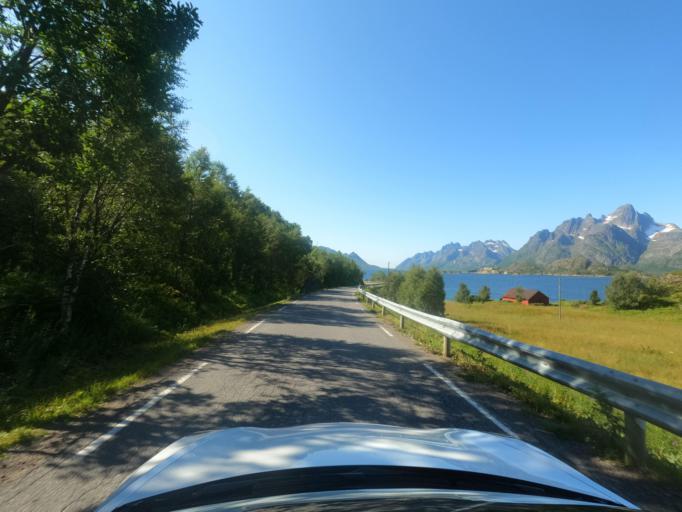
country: NO
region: Nordland
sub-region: Hadsel
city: Stokmarknes
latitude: 68.3469
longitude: 15.0550
